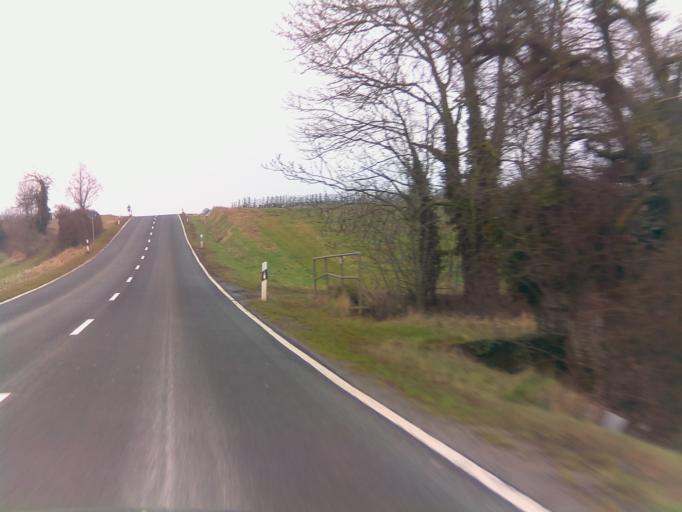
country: DE
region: Rheinland-Pfalz
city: Flomborn
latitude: 49.6944
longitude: 8.1441
